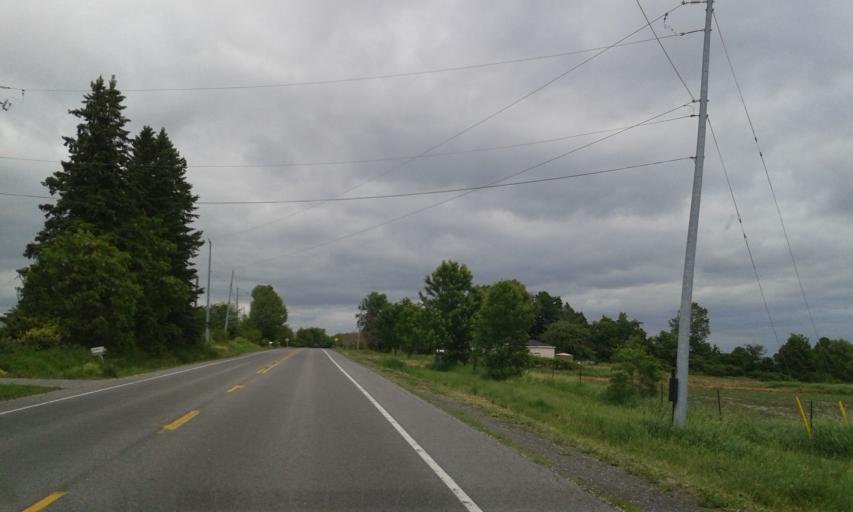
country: CA
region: Ontario
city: Deseronto
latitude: 44.0991
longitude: -76.9408
